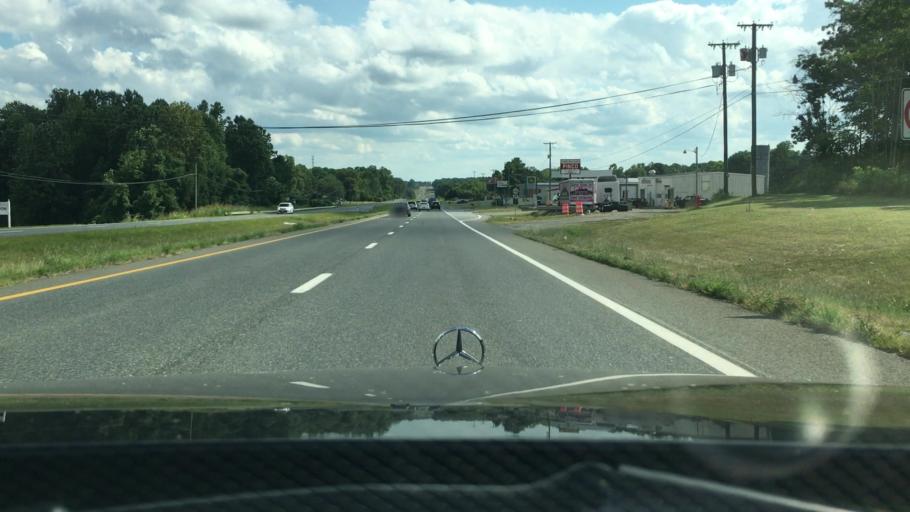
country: US
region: Virginia
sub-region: Campbell County
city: Rustburg
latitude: 37.2744
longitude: -79.1724
